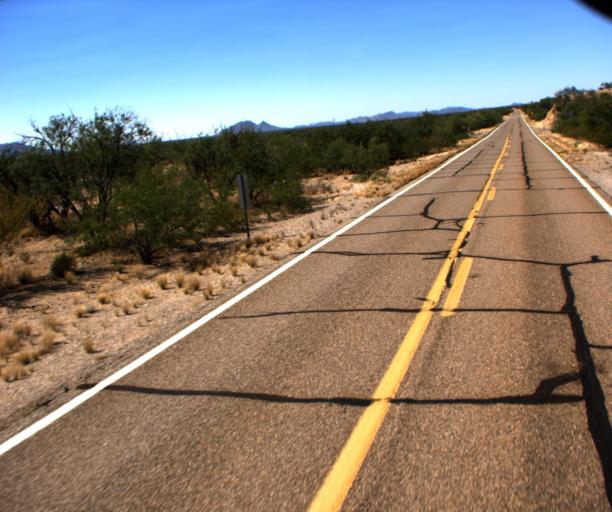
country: US
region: Arizona
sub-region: Pima County
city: Three Points
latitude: 31.8988
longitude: -111.3919
